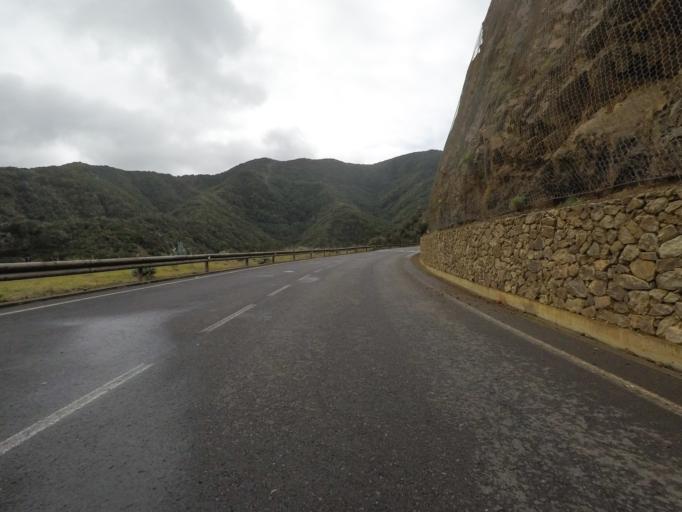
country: ES
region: Canary Islands
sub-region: Provincia de Santa Cruz de Tenerife
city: Vallehermosa
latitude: 28.1604
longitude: -17.2850
